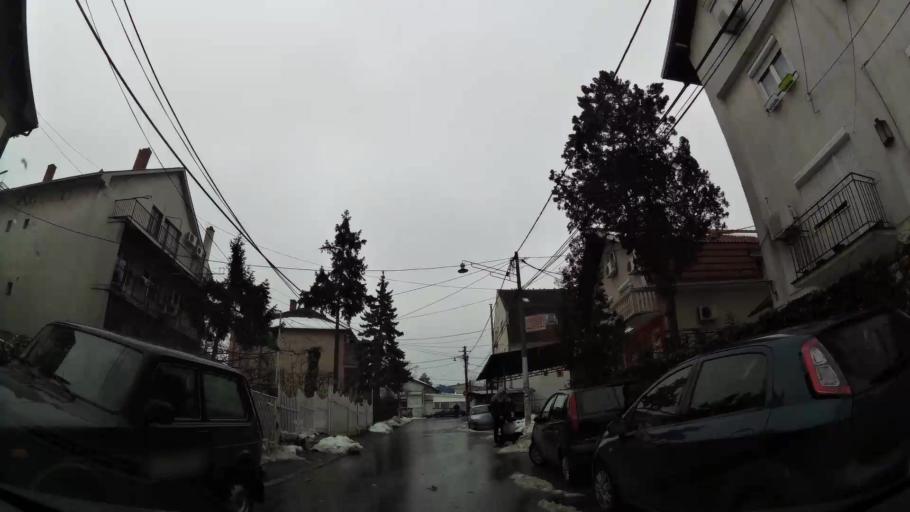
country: RS
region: Central Serbia
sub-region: Belgrade
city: Vozdovac
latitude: 44.7449
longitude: 20.5010
